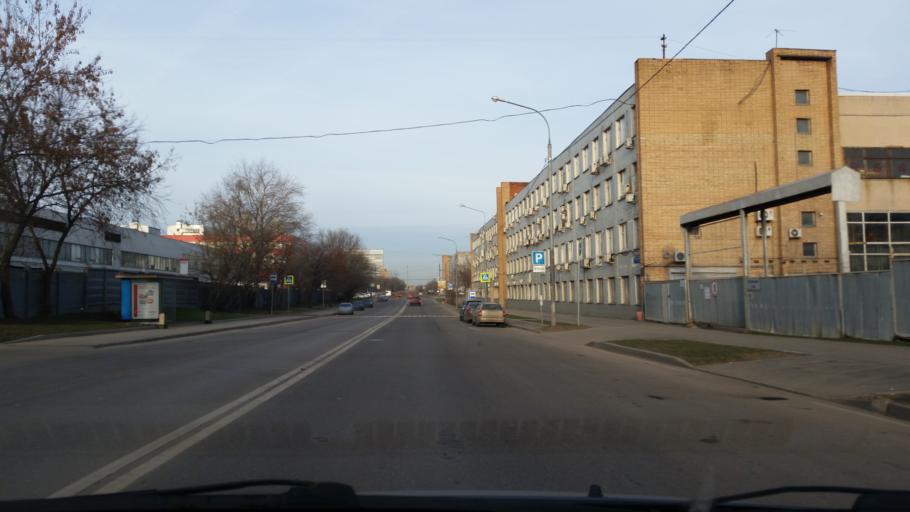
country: RU
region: Moscow
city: Chertanovo Yuzhnoye
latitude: 55.6128
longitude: 37.6181
